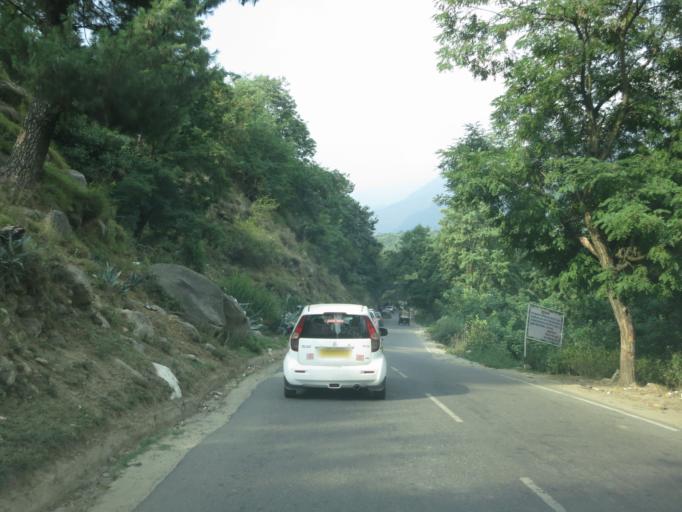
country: IN
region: Himachal Pradesh
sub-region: Kulu
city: Nagar
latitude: 32.1113
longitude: 77.1452
